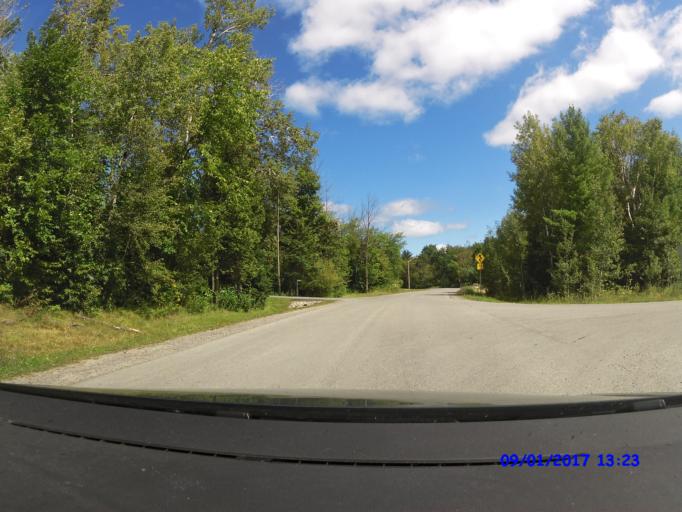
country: CA
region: Ontario
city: Bells Corners
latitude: 45.3437
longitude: -75.9943
